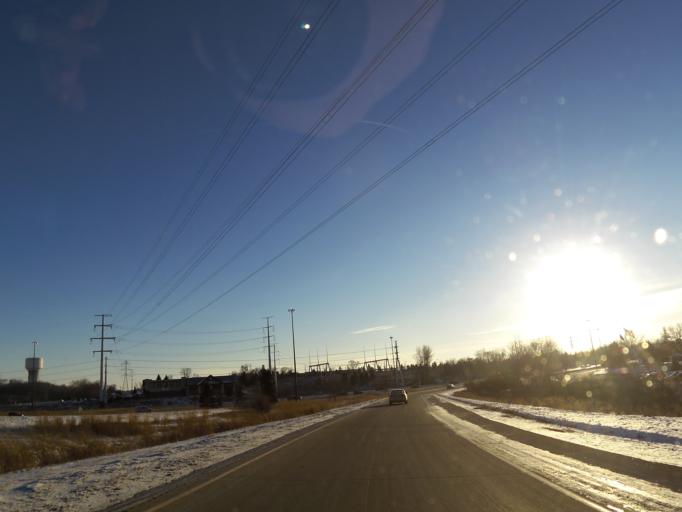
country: US
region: Minnesota
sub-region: Hennepin County
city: Eden Prairie
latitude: 44.8661
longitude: -93.4326
